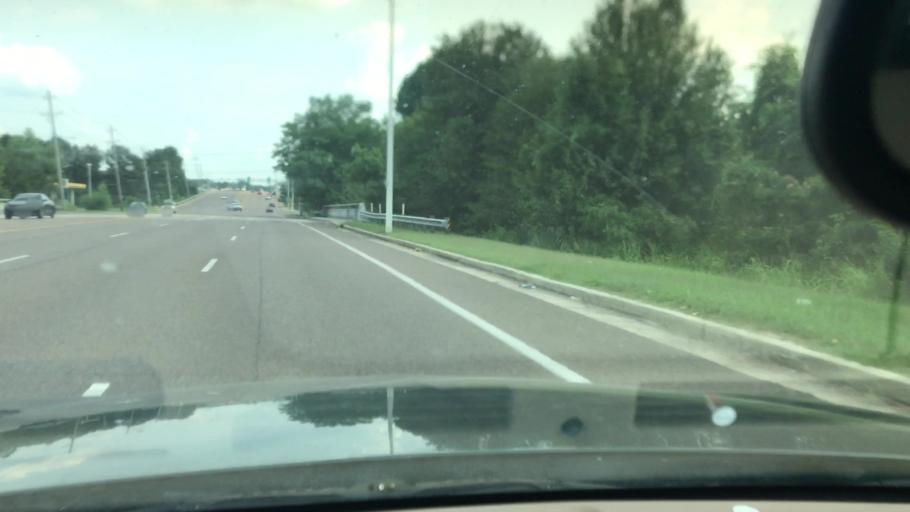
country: US
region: Tennessee
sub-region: Shelby County
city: Bartlett
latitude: 35.1908
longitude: -89.8148
